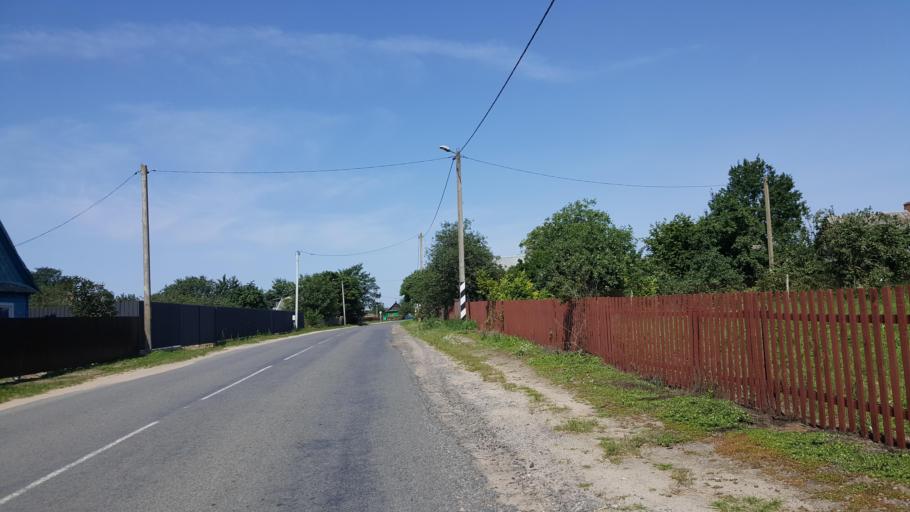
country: BY
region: Brest
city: Vysokaye
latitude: 52.3638
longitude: 23.5301
